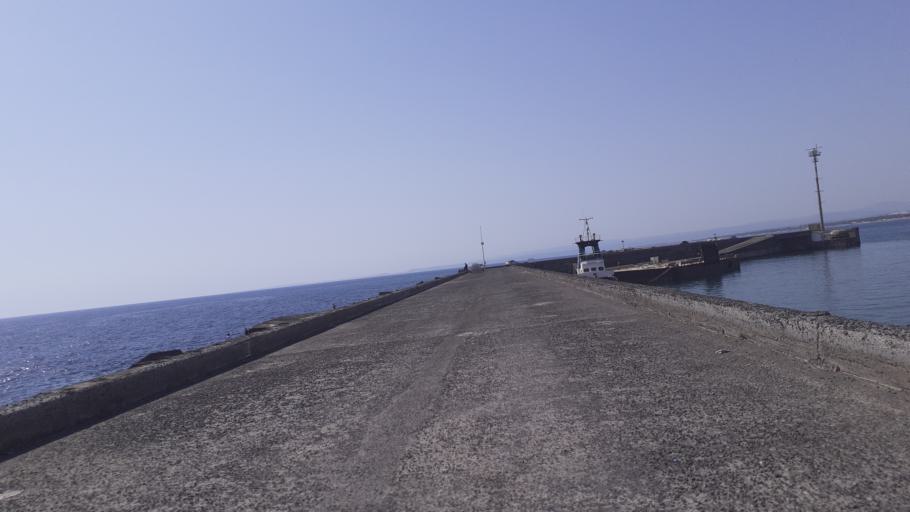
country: IT
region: Sicily
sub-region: Catania
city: Catania
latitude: 37.4897
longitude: 15.1000
